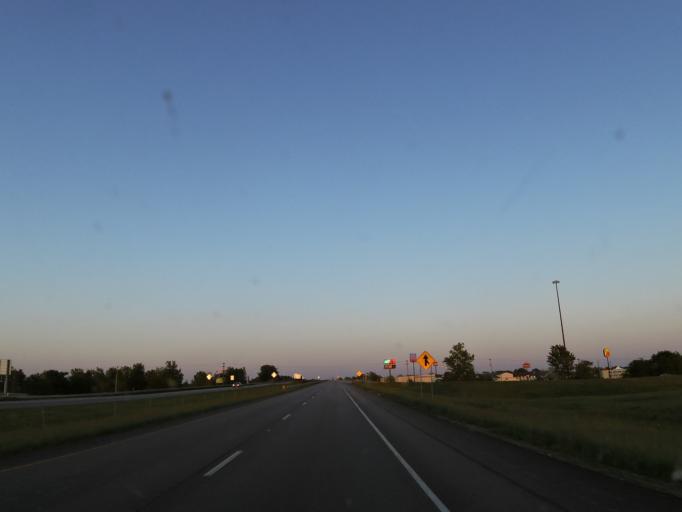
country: US
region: Indiana
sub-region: Montgomery County
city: Crawfordsville
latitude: 40.0801
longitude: -86.9073
